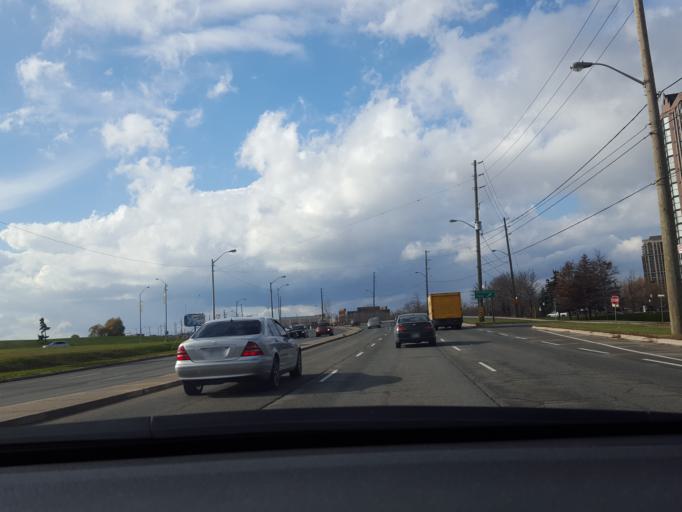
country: CA
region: Ontario
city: Etobicoke
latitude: 43.7204
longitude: -79.6086
